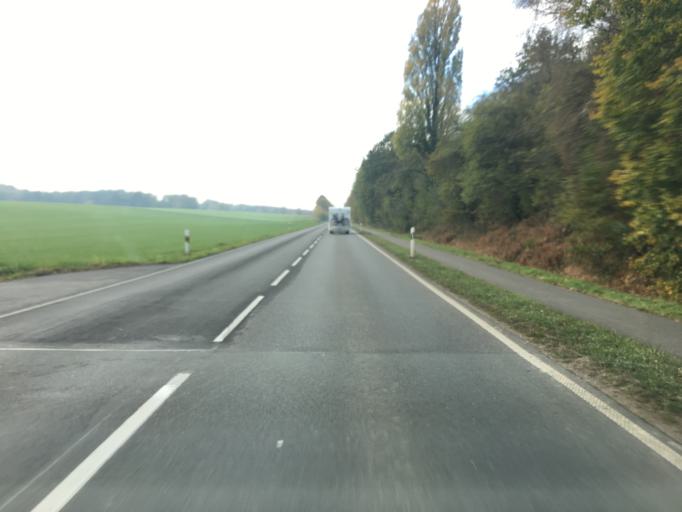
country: DE
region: North Rhine-Westphalia
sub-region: Regierungsbezirk Dusseldorf
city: Sonsbeck
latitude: 51.6322
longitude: 6.4039
